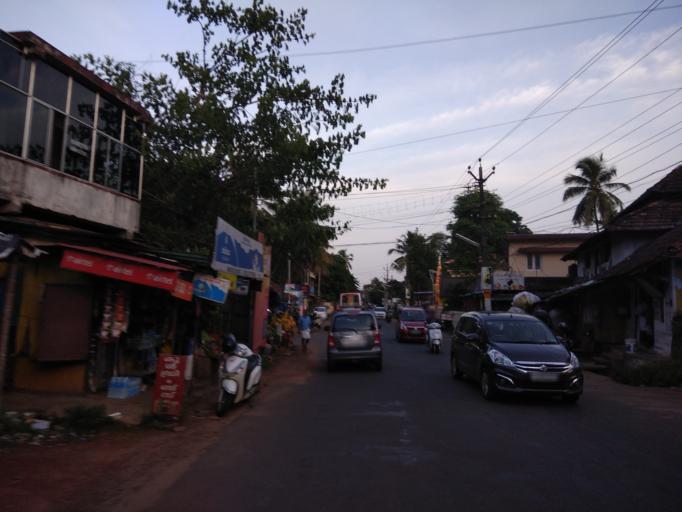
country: IN
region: Kerala
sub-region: Thrissur District
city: Trichur
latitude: 10.5305
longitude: 76.1854
